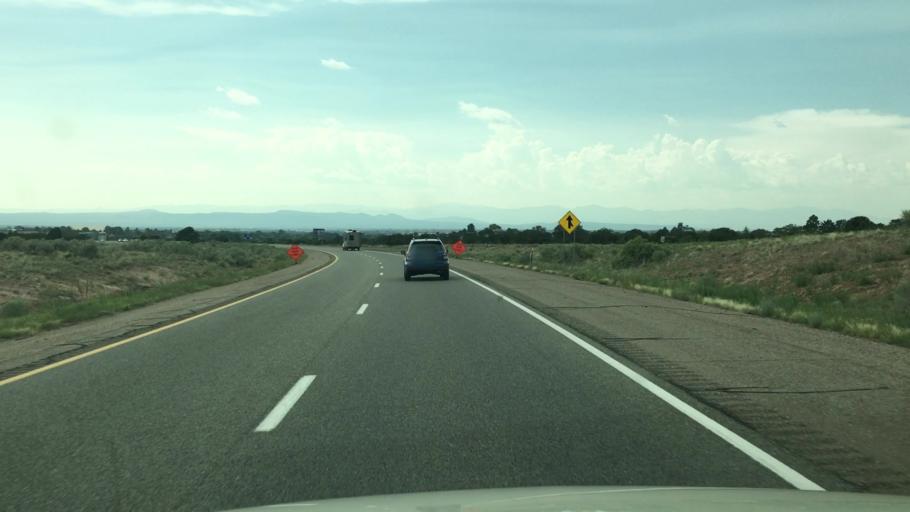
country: US
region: New Mexico
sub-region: Santa Fe County
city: Santa Fe
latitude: 35.6372
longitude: -105.9317
